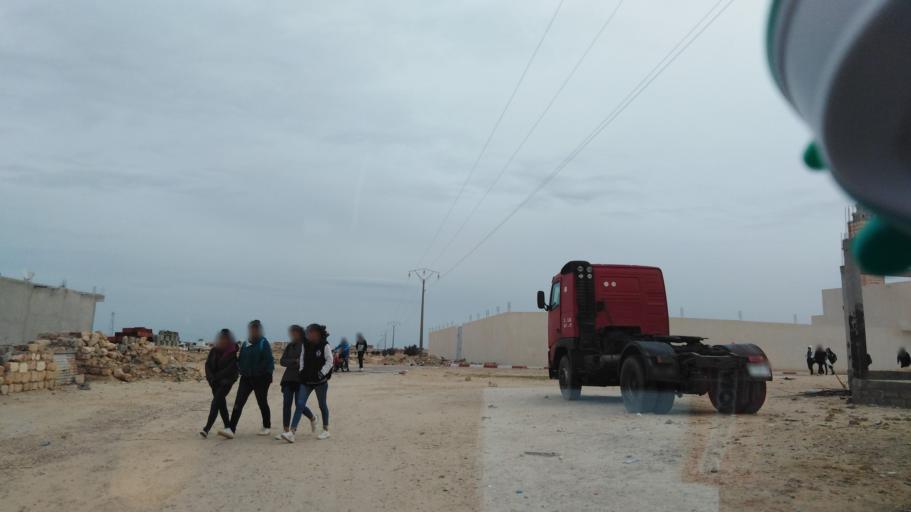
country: TN
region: Qabis
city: Gabes
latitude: 33.9516
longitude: 10.0046
